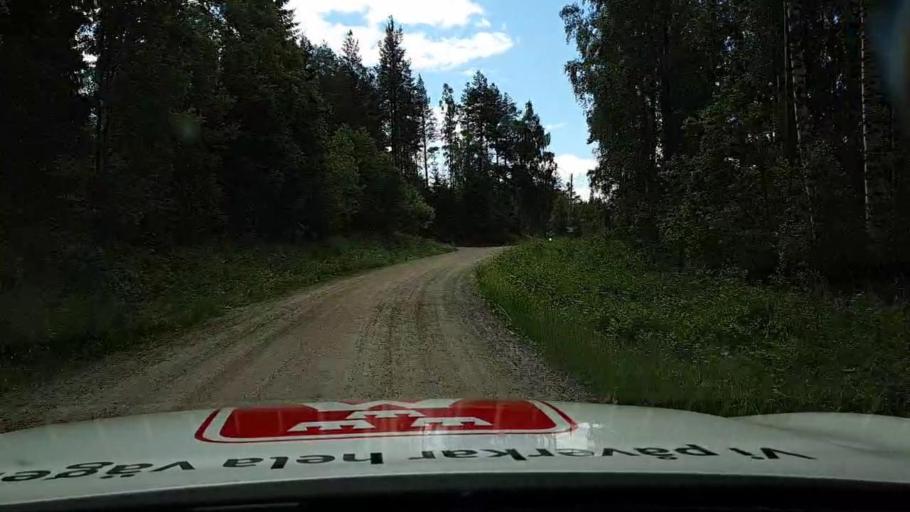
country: SE
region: Jaemtland
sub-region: Braecke Kommun
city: Braecke
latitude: 62.7561
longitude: 15.5032
